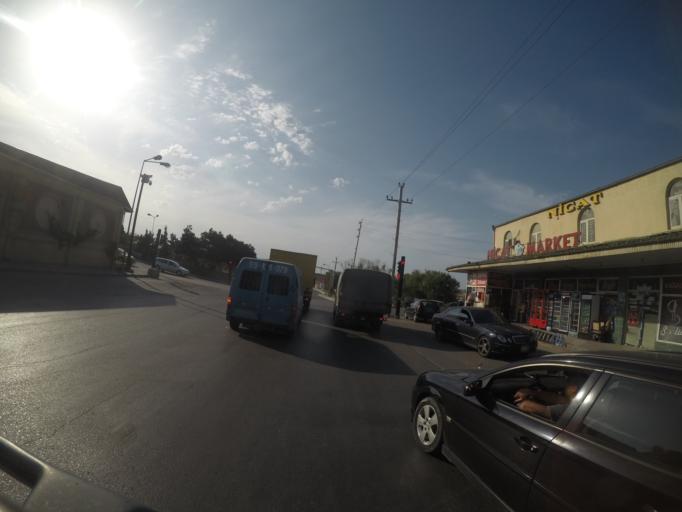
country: AZ
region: Baki
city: Binagadi
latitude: 40.4725
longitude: 49.8358
